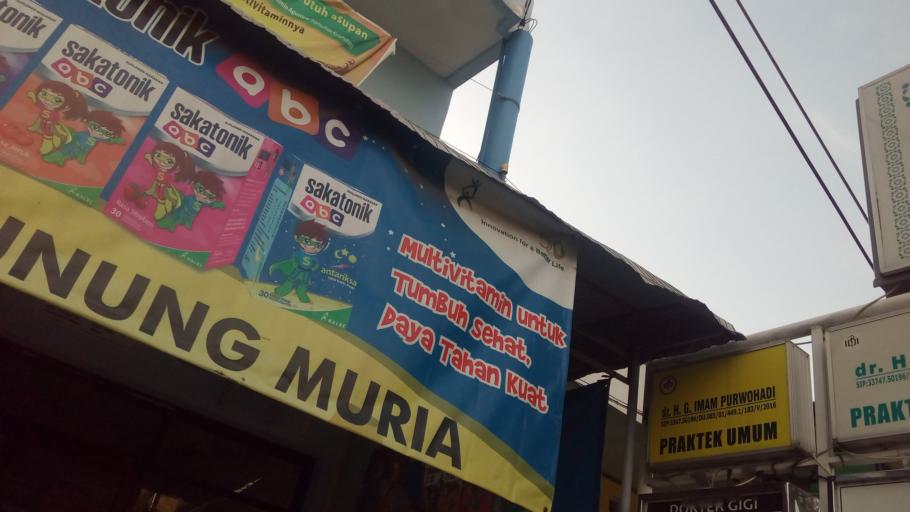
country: ID
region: Central Java
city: Semarang
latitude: -6.9922
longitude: 110.4730
